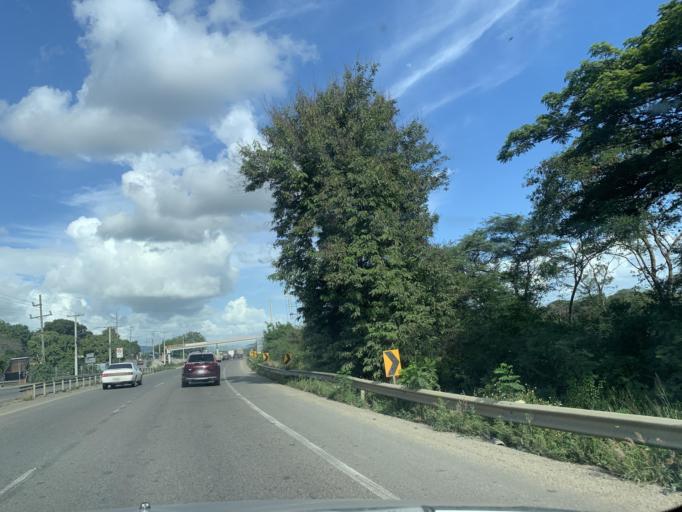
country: DO
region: Santiago
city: Villa Gonzalez
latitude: 19.5532
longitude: -70.8214
